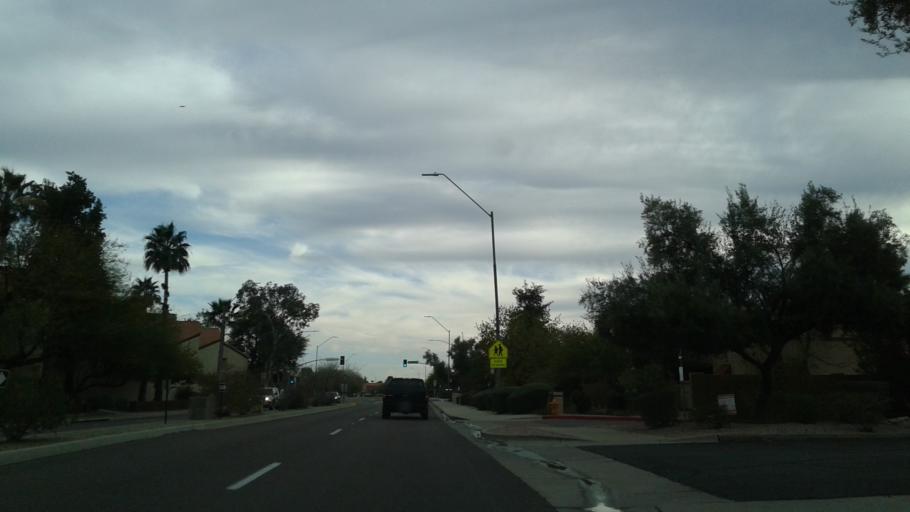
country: US
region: Arizona
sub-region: Maricopa County
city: Paradise Valley
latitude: 33.5799
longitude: -111.9305
